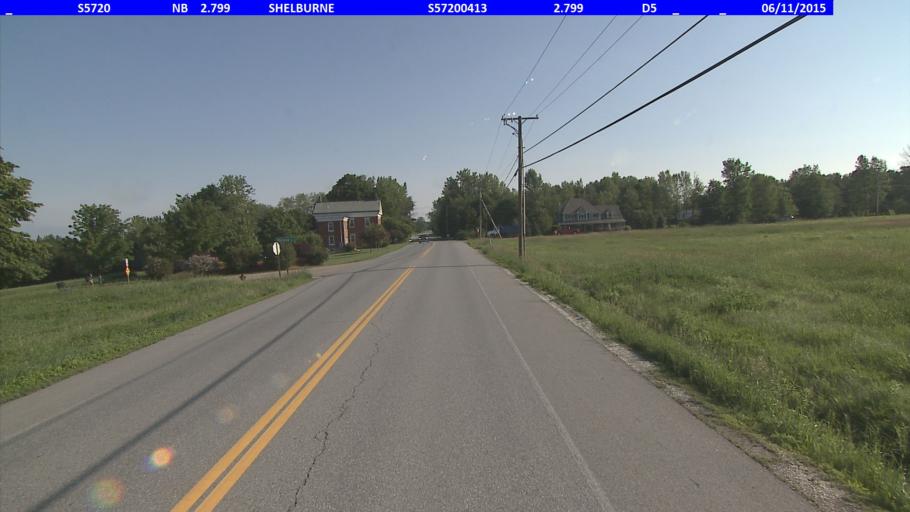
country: US
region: Vermont
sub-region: Chittenden County
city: South Burlington
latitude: 44.4078
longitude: -73.1979
